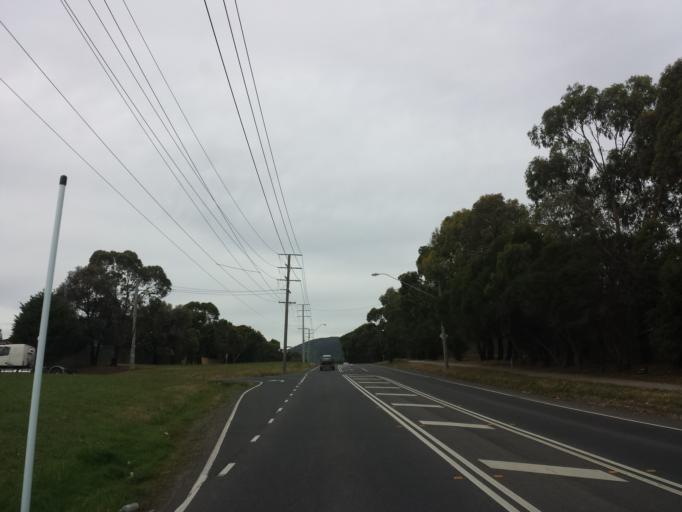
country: AU
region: Victoria
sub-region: Knox
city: Ferntree Gully
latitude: -37.9098
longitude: 145.2761
